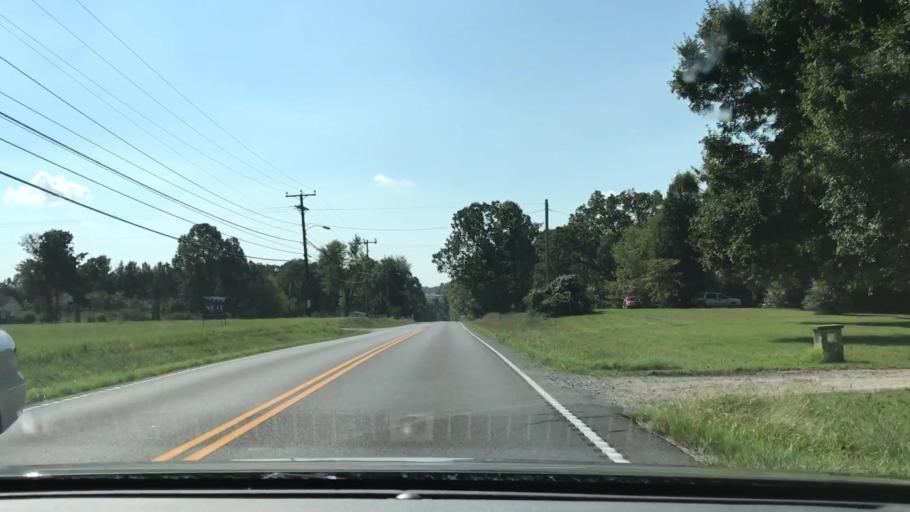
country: US
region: Kentucky
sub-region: Marshall County
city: Benton
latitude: 36.8293
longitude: -88.3506
